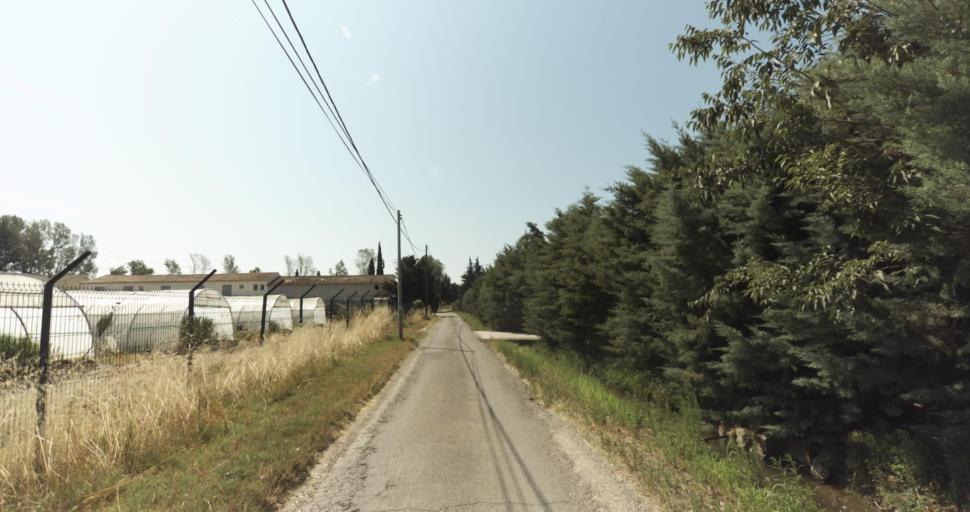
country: FR
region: Provence-Alpes-Cote d'Azur
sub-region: Departement du Vaucluse
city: Monteux
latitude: 44.0238
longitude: 5.0098
